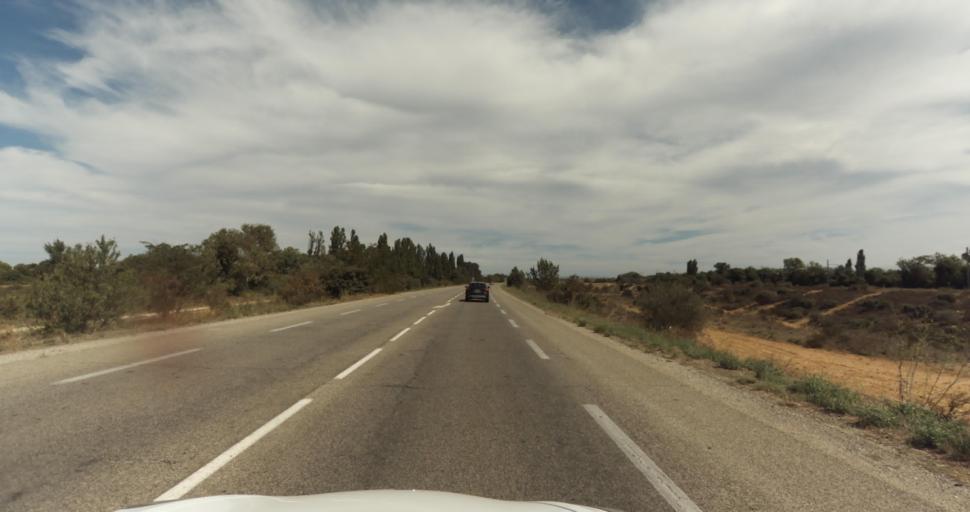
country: FR
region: Provence-Alpes-Cote d'Azur
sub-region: Departement des Bouches-du-Rhone
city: Istres
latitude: 43.5519
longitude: 4.9584
